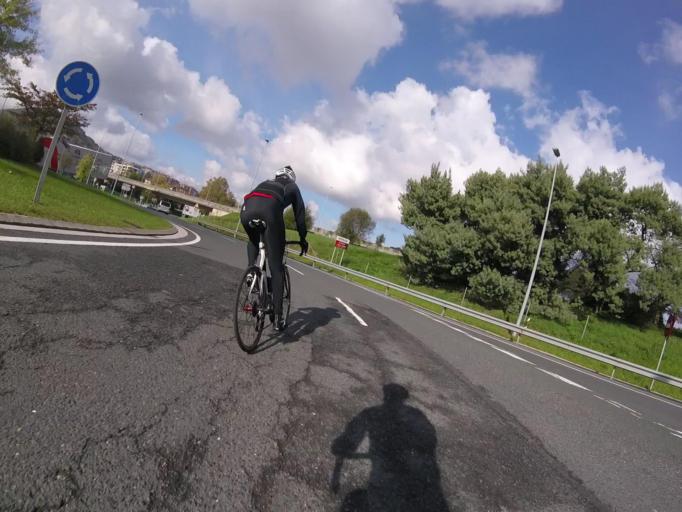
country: ES
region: Basque Country
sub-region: Provincia de Guipuzcoa
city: Hernani
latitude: 43.2648
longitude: -1.9671
